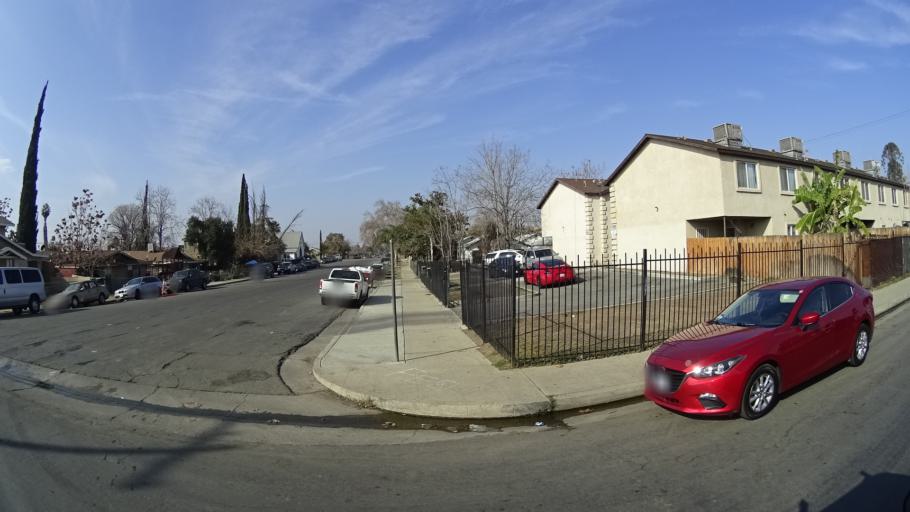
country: US
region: California
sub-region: Kern County
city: Bakersfield
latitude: 35.3812
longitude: -118.9728
